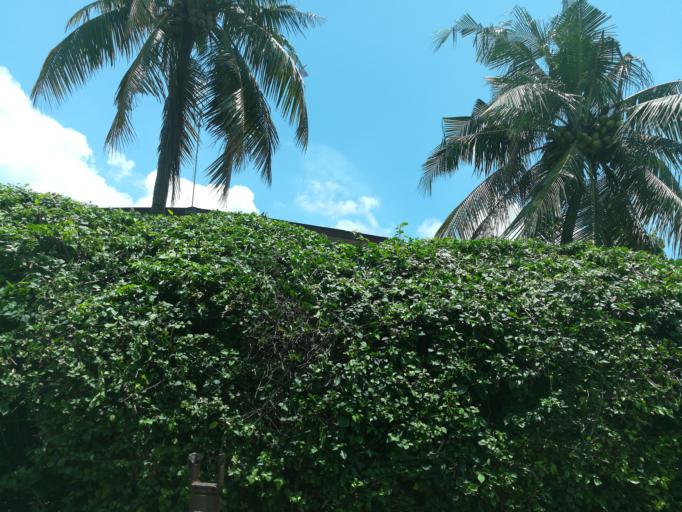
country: NG
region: Lagos
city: Ikorodu
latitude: 6.6077
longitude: 3.4985
